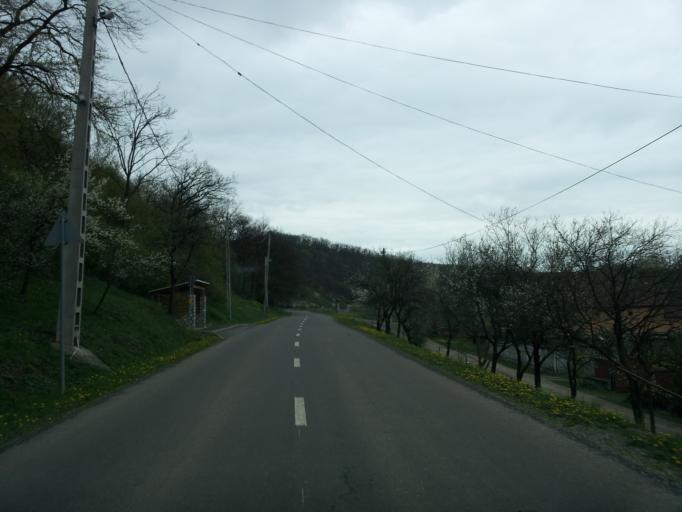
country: HU
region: Borsod-Abauj-Zemplen
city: Rudabanya
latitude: 48.4881
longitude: 20.6283
